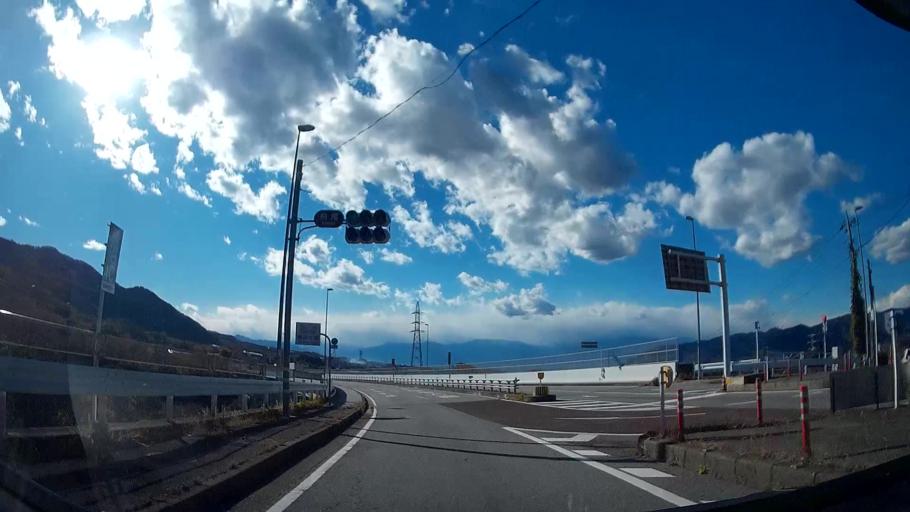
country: JP
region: Yamanashi
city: Enzan
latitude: 35.6568
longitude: 138.7394
